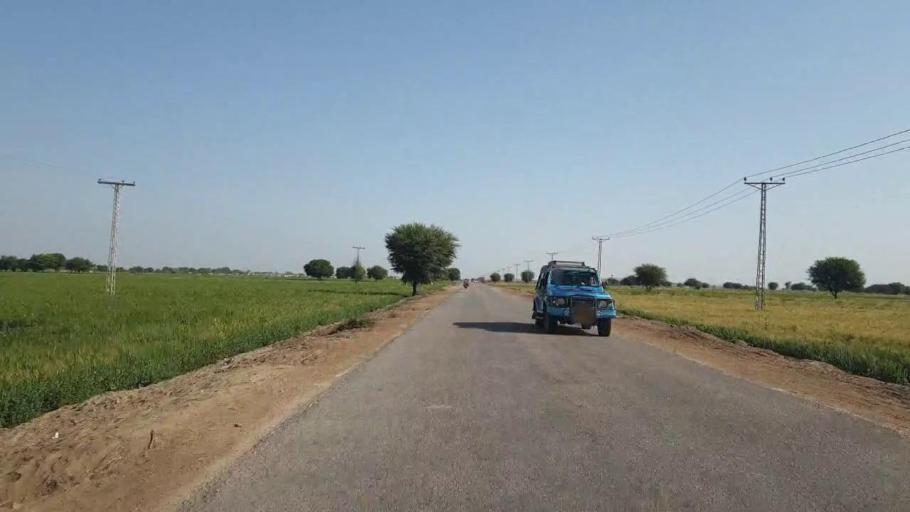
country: PK
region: Sindh
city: Umarkot
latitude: 25.4152
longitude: 69.7317
